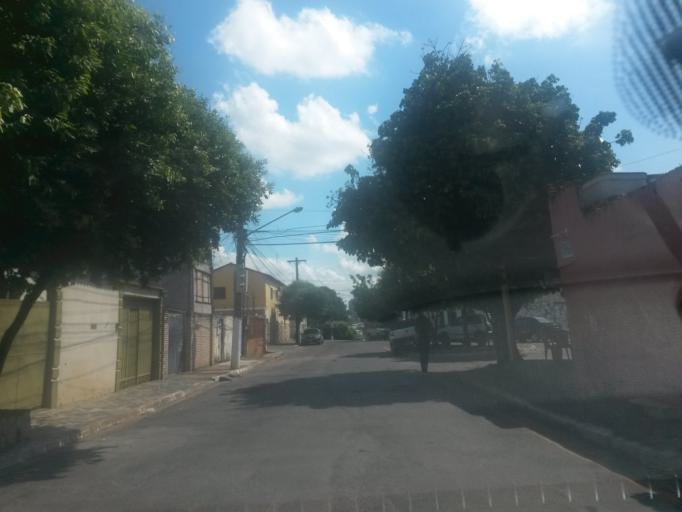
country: BR
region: Mato Grosso
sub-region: Cuiaba
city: Cuiaba
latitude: -15.5948
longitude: -56.0878
